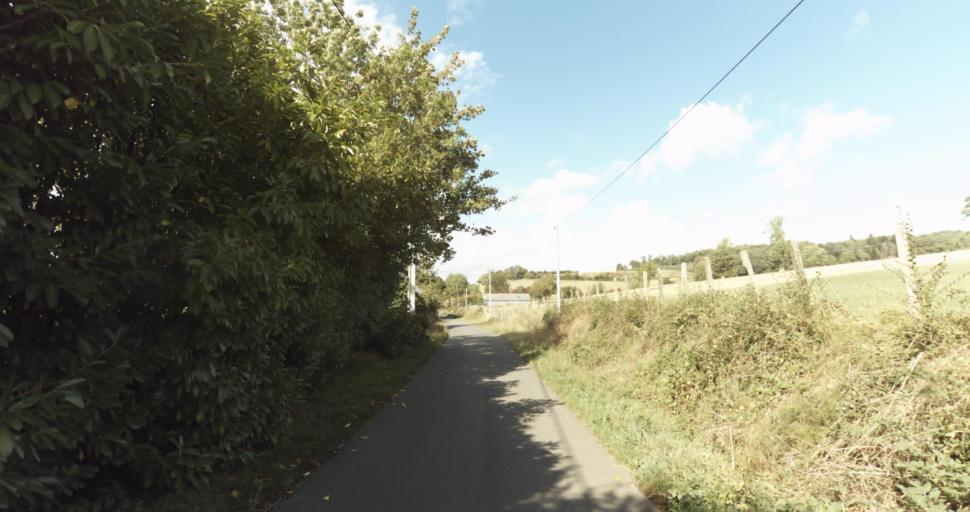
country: FR
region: Lower Normandy
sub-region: Departement de l'Orne
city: Gace
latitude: 48.7796
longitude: 0.3070
